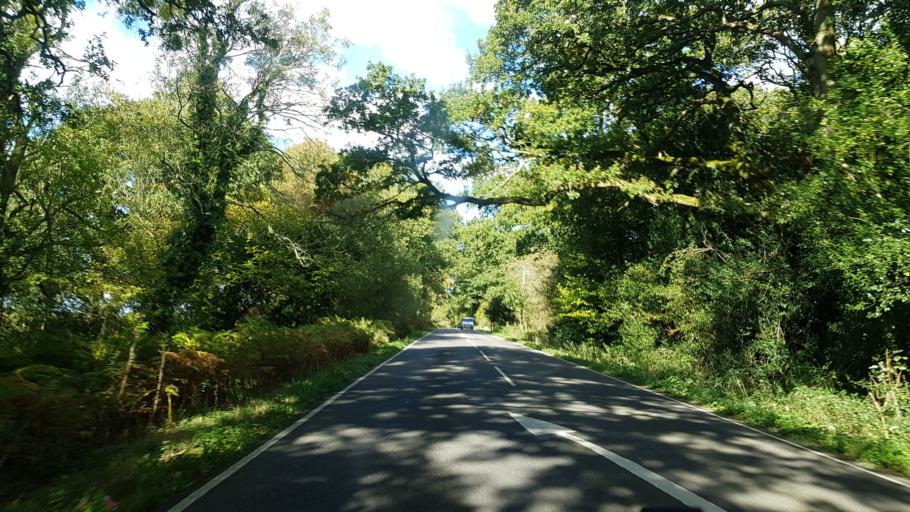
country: GB
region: England
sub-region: West Sussex
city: Petworth
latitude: 51.0180
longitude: -0.6243
